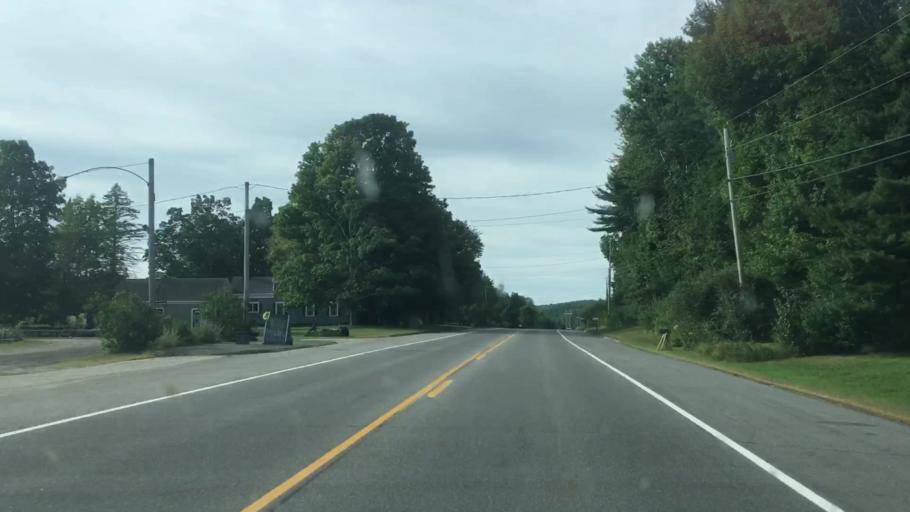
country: US
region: Maine
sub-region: Cumberland County
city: Cumberland Center
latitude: 43.7652
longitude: -70.3009
